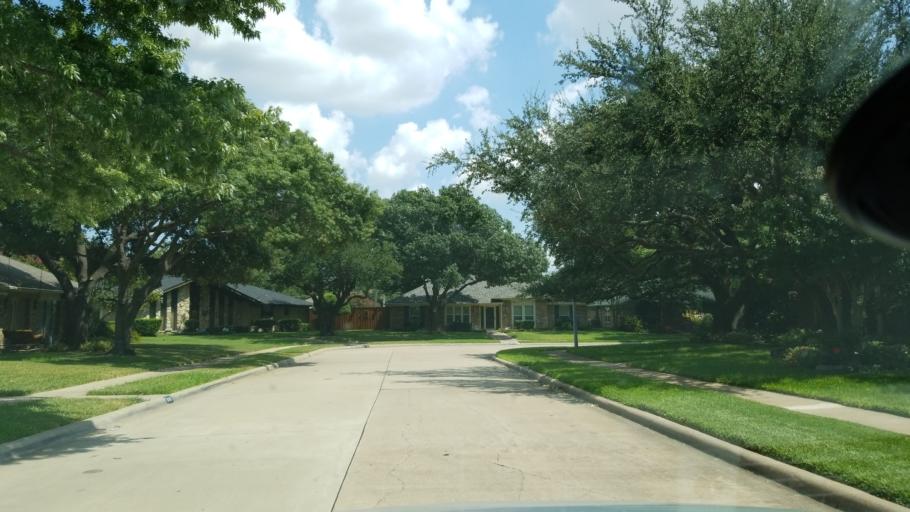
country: US
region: Texas
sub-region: Dallas County
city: Richardson
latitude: 32.9268
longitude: -96.7193
